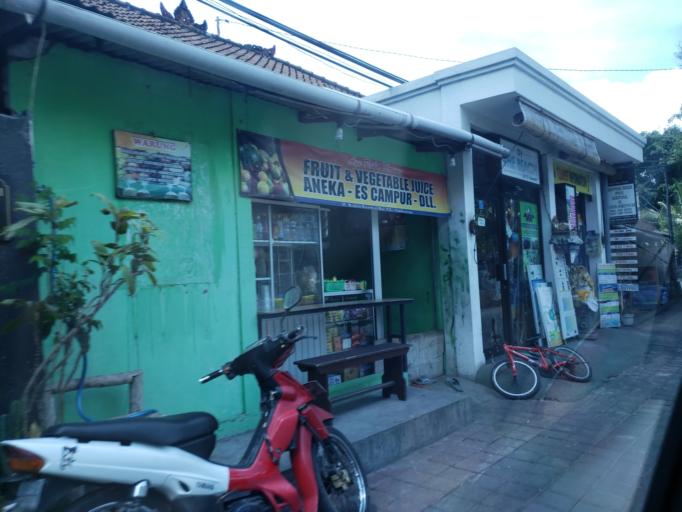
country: ID
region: Bali
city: Jimbaran
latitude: -8.7827
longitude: 115.1658
